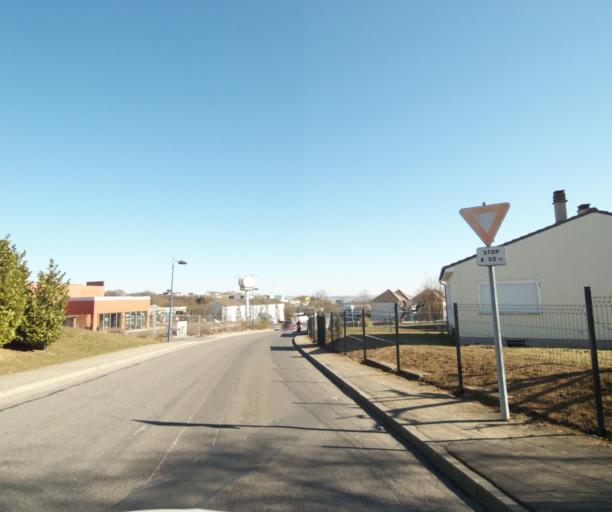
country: FR
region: Lorraine
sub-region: Departement de Meurthe-et-Moselle
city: Ludres
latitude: 48.6156
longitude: 6.1753
